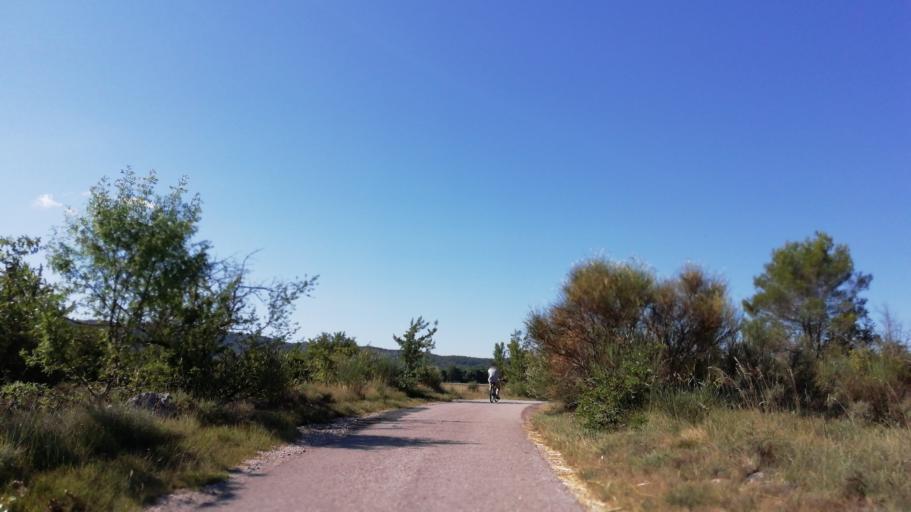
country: FR
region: Languedoc-Roussillon
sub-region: Departement de l'Herault
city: Saint-Martin-de-Londres
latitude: 43.8045
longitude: 3.7611
